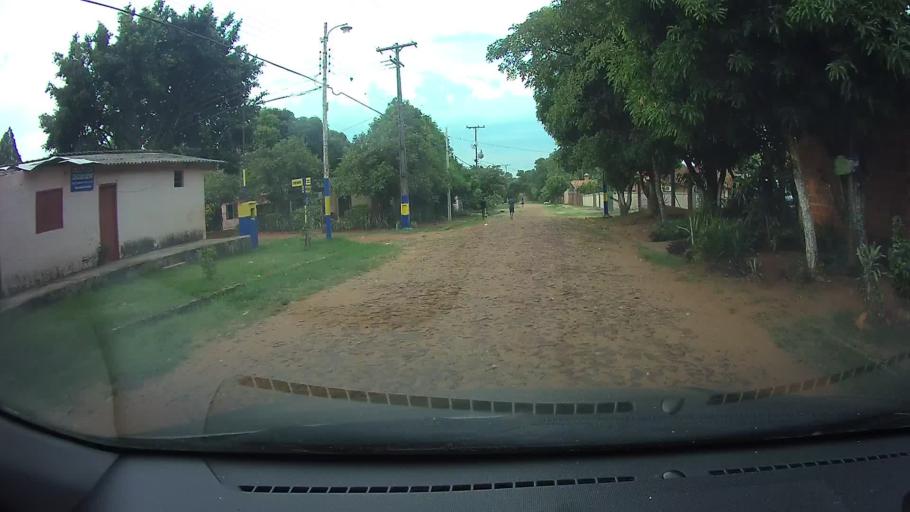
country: PY
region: Central
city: San Lorenzo
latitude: -25.2611
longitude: -57.4633
